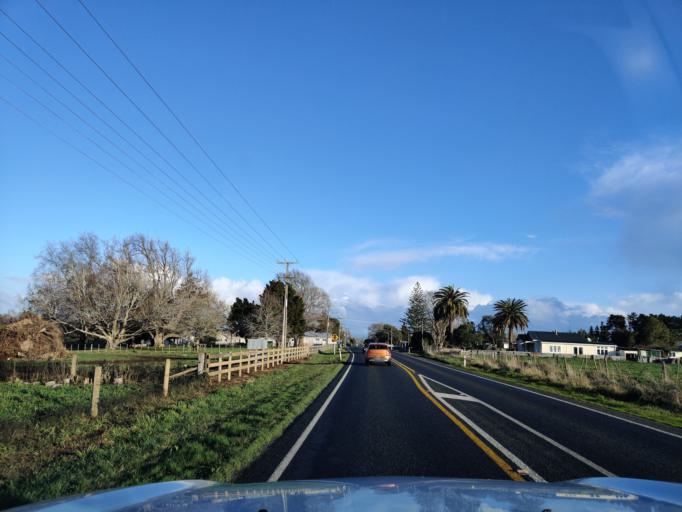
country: NZ
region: Waikato
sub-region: Hauraki District
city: Paeroa
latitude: -37.5878
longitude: 175.5020
